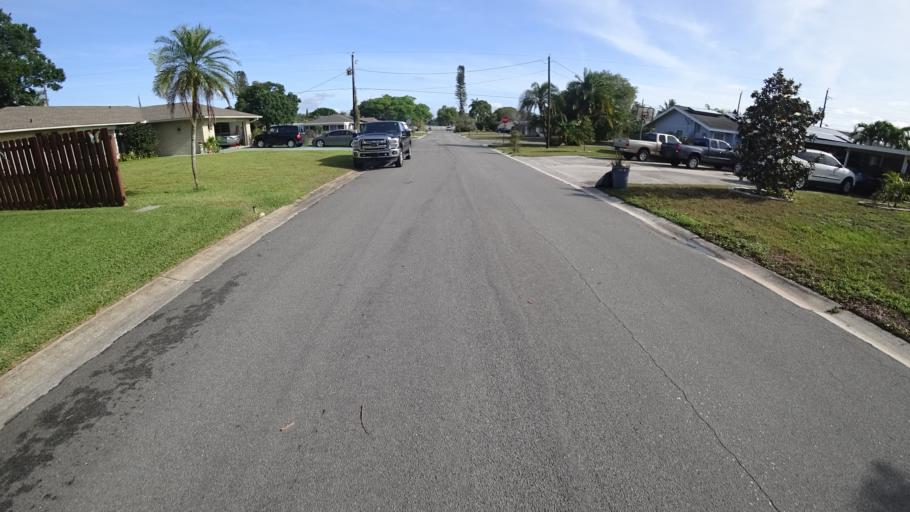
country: US
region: Florida
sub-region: Manatee County
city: West Bradenton
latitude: 27.5010
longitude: -82.6214
